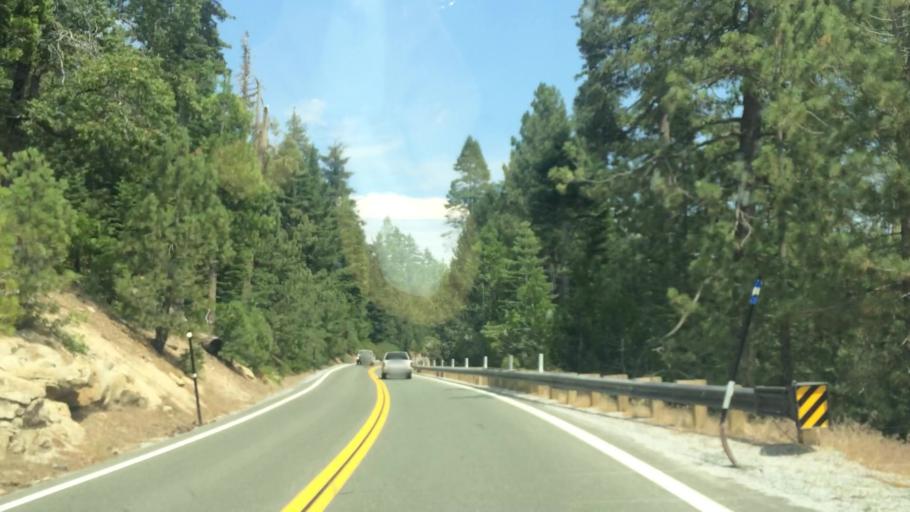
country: US
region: California
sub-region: Amador County
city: Pioneer
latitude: 38.5447
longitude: -120.3325
